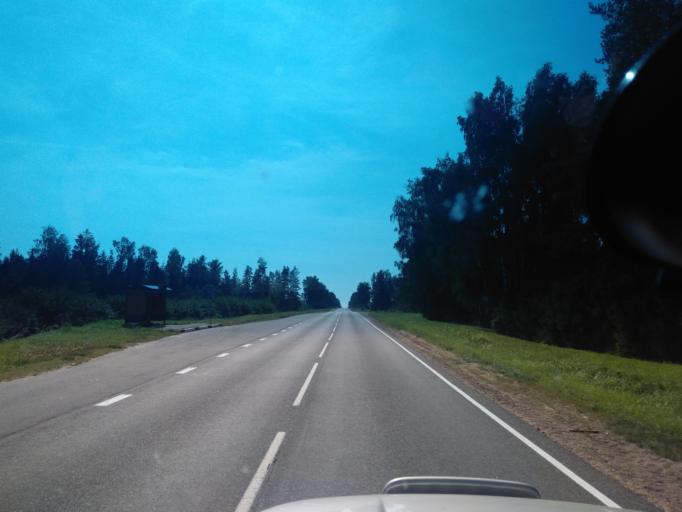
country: BY
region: Minsk
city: Uzda
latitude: 53.3542
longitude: 27.2255
